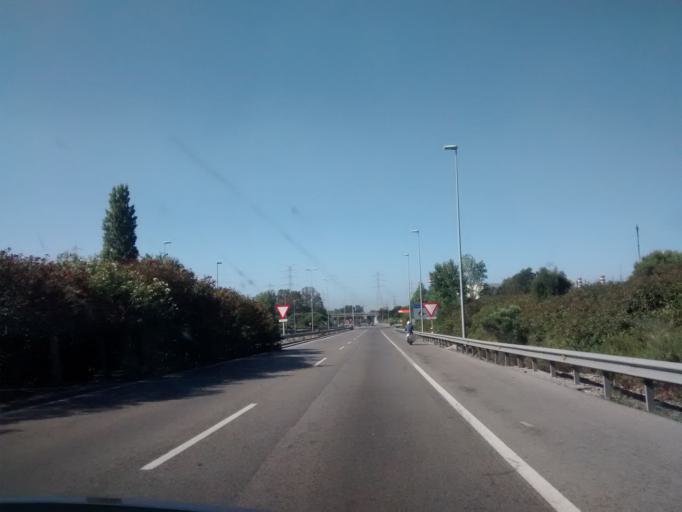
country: ES
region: Andalusia
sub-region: Provincia de Cadiz
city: San Roque
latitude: 36.1935
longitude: -5.3845
